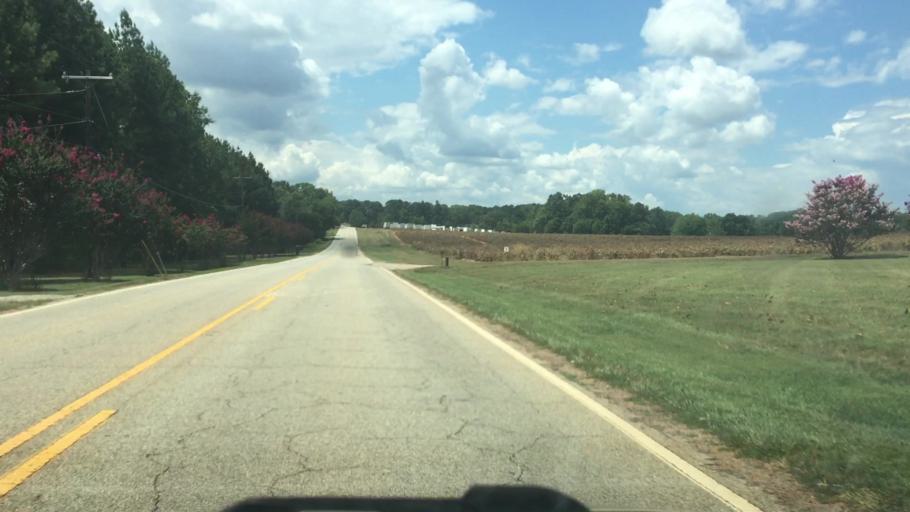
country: US
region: North Carolina
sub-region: Rowan County
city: Landis
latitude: 35.6209
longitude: -80.6494
